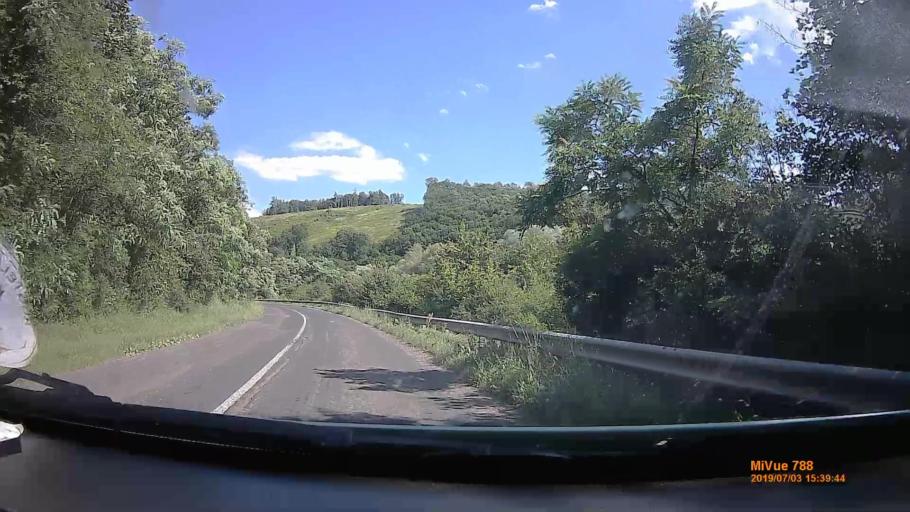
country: HU
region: Heves
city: Szilvasvarad
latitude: 48.1635
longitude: 20.4037
